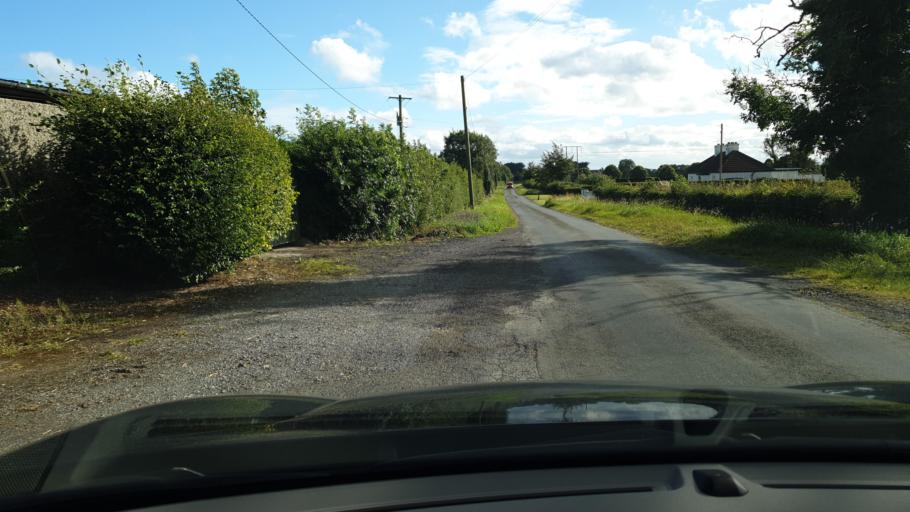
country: IE
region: Leinster
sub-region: An Mhi
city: Ashbourne
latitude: 53.4590
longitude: -6.4227
